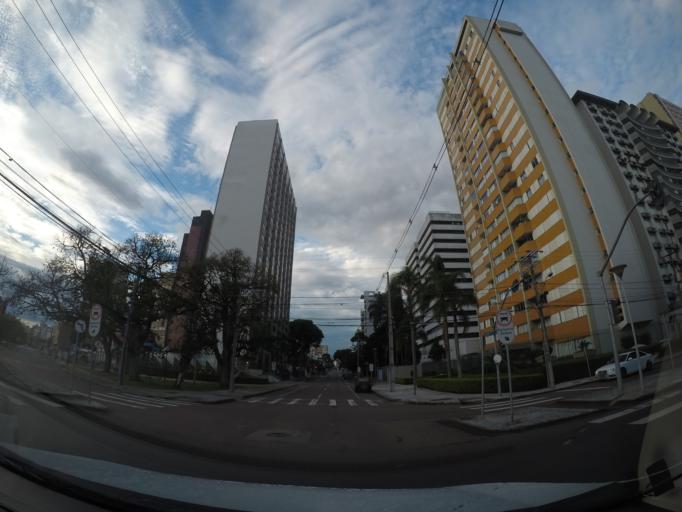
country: BR
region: Parana
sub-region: Curitiba
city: Curitiba
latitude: -25.4288
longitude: -49.2886
